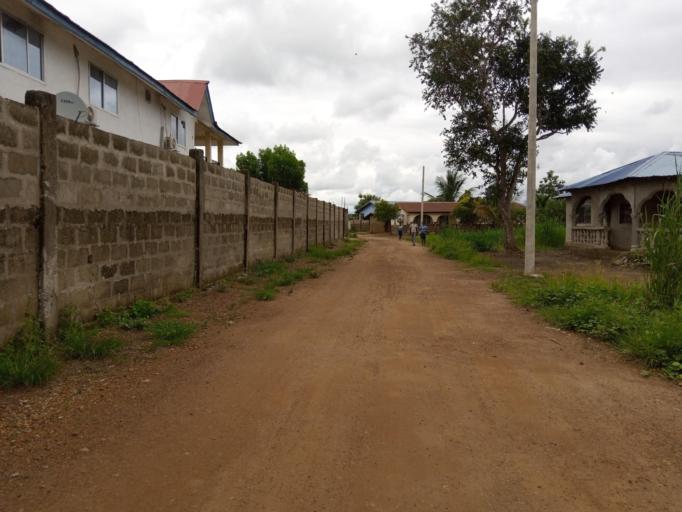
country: SL
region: Southern Province
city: Moyamba
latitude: 8.1680
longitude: -12.4212
